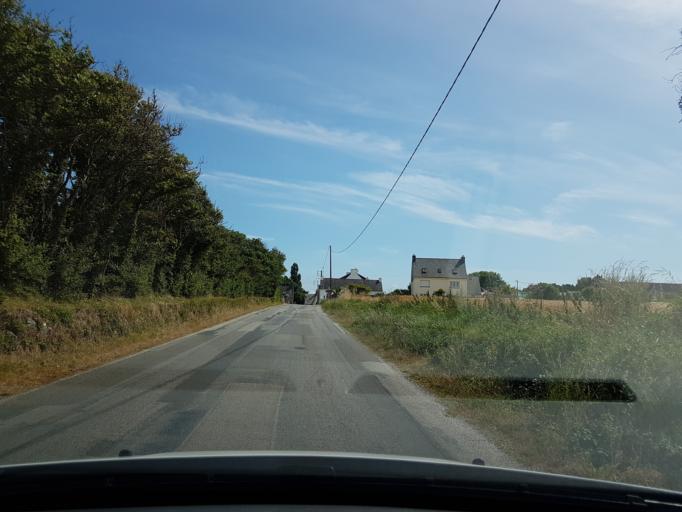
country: FR
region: Brittany
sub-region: Departement du Morbihan
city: Etel
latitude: 47.6724
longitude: -3.2210
